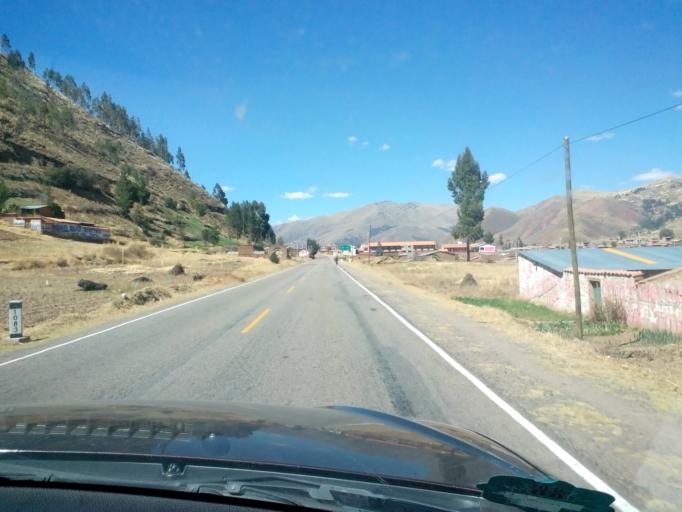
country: PE
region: Cusco
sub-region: Provincia de Canchis
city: Tinta
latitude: -14.1377
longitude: -71.4043
